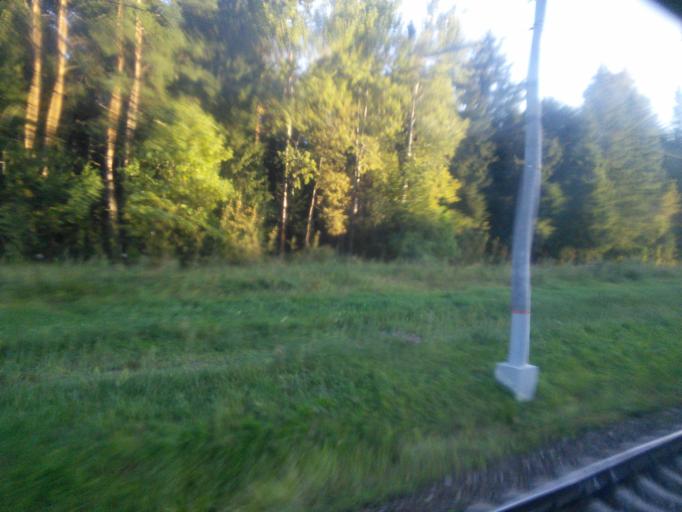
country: RU
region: Moskovskaya
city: Rakhmanovo
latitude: 55.7523
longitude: 38.5544
